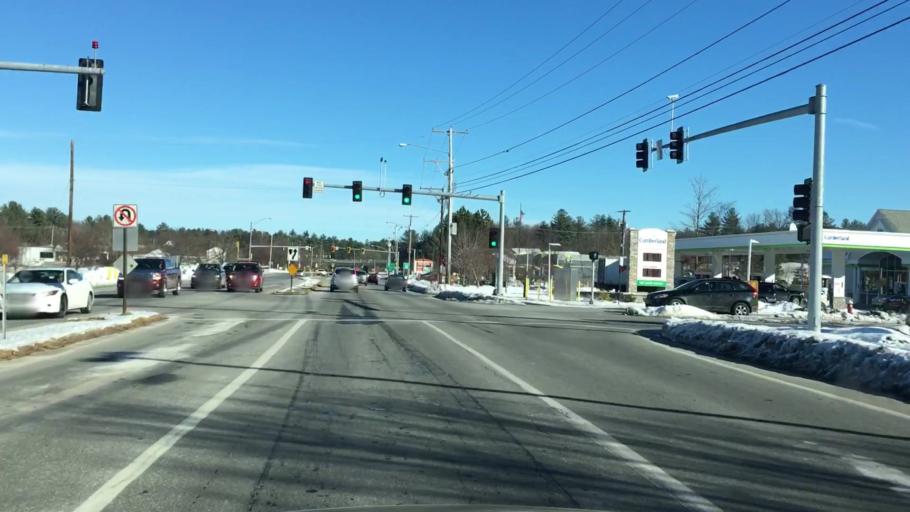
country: US
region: New Hampshire
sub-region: Hillsborough County
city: Milford
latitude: 42.8235
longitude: -71.6245
